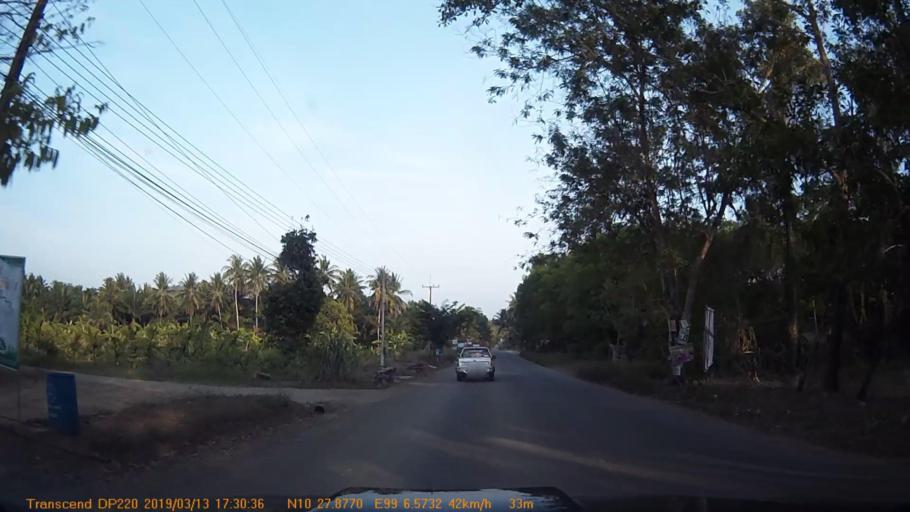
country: TH
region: Chumphon
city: Chumphon
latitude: 10.4645
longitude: 99.1099
